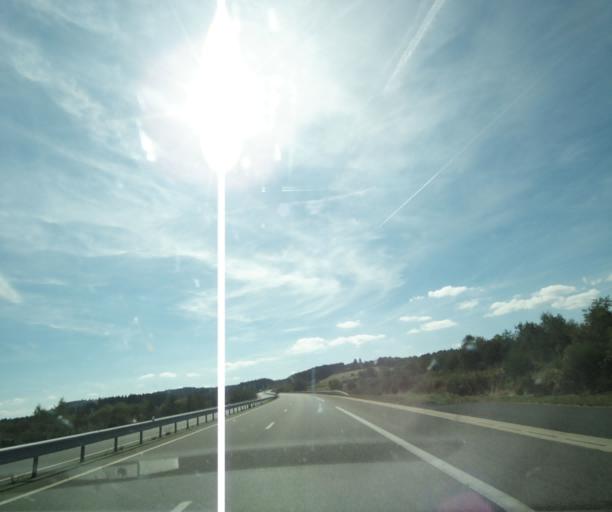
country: FR
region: Auvergne
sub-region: Departement du Puy-de-Dome
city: Gelles
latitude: 45.7676
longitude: 2.7311
